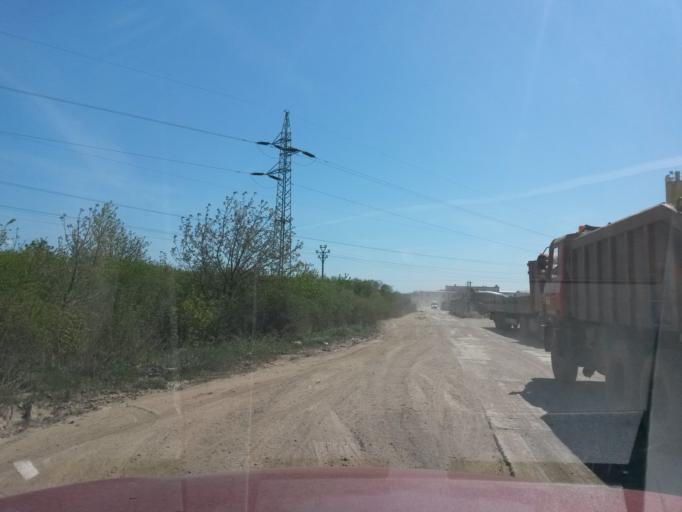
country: SK
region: Kosicky
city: Kosice
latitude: 48.6756
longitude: 21.2762
